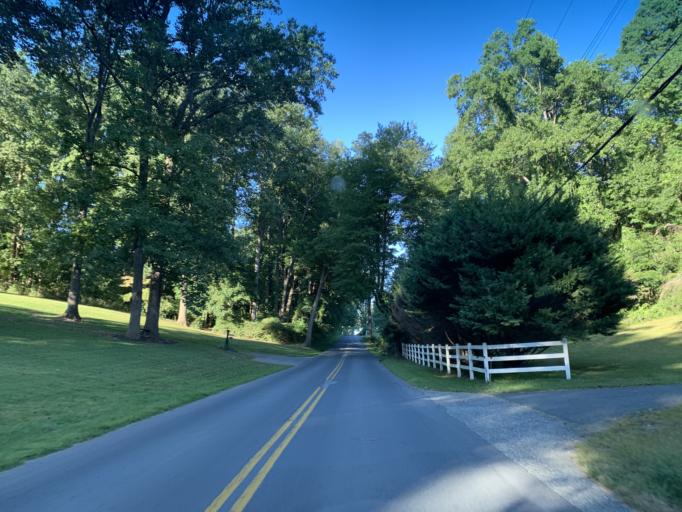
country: US
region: Maryland
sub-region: Harford County
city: Jarrettsville
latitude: 39.5896
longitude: -76.4470
